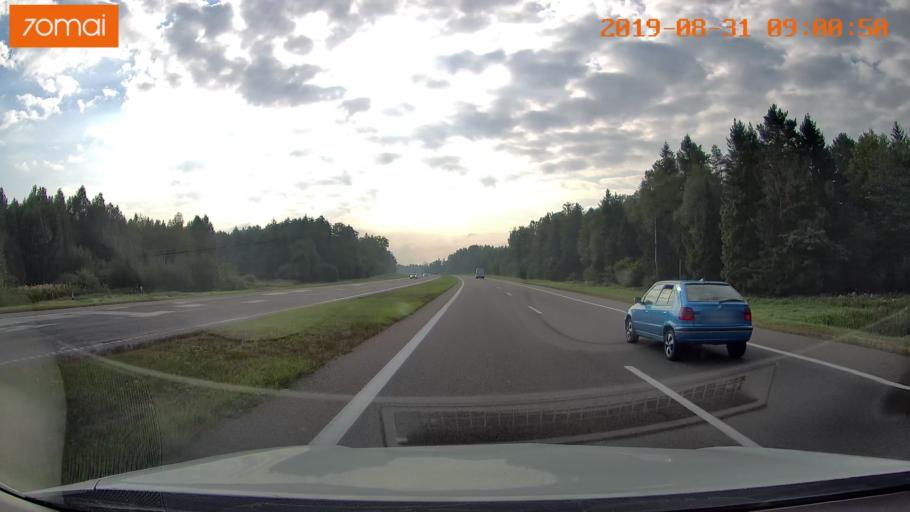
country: BY
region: Minsk
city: Chervyen'
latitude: 53.7533
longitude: 28.2457
